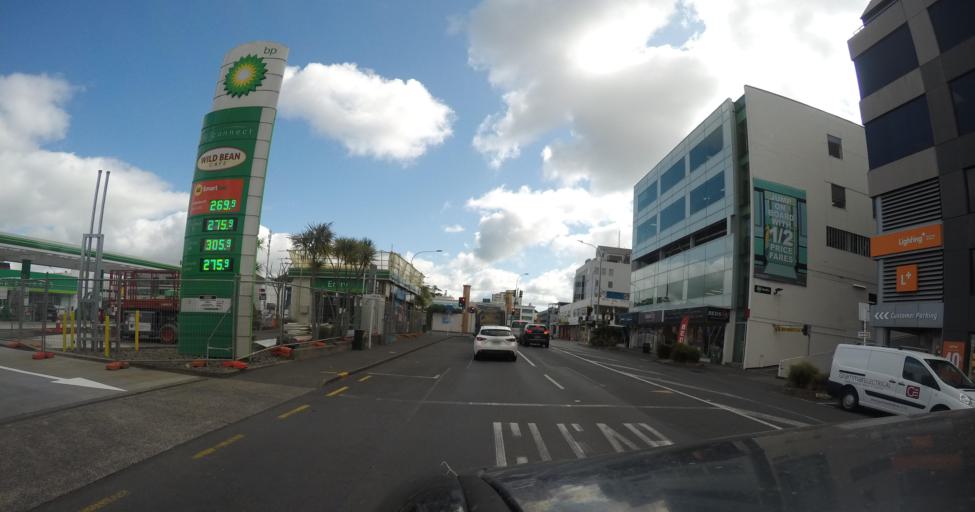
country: NZ
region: Auckland
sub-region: Auckland
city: Auckland
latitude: -36.8676
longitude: 174.7753
